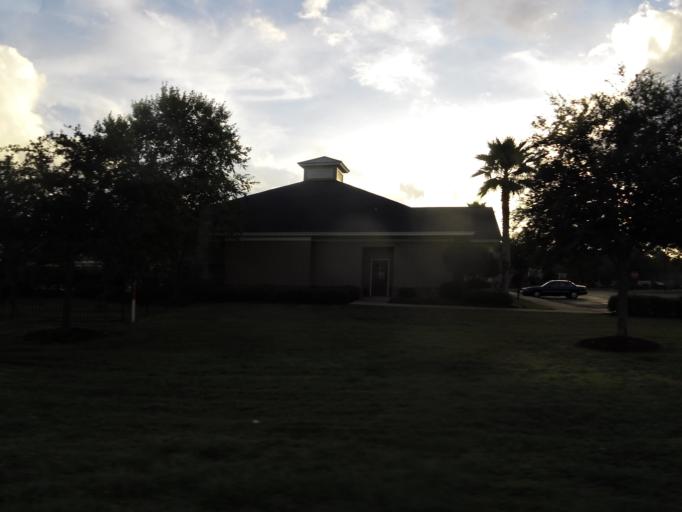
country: US
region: Georgia
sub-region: Glynn County
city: Country Club Estates
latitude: 31.2120
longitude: -81.4837
